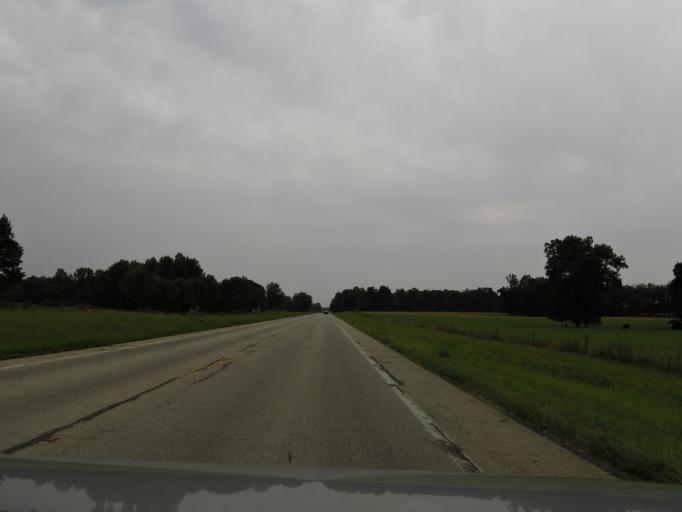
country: US
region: Ohio
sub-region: Brown County
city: Ripley
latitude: 38.8194
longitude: -83.8155
